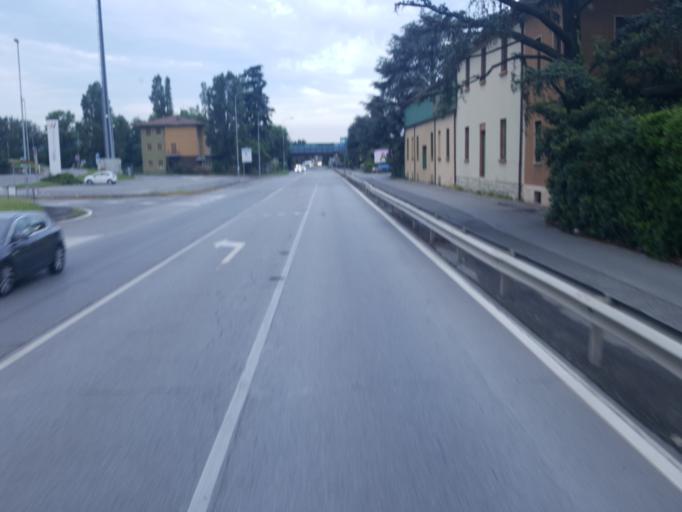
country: IT
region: Lombardy
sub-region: Provincia di Brescia
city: Roncadelle
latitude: 45.5290
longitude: 10.1640
